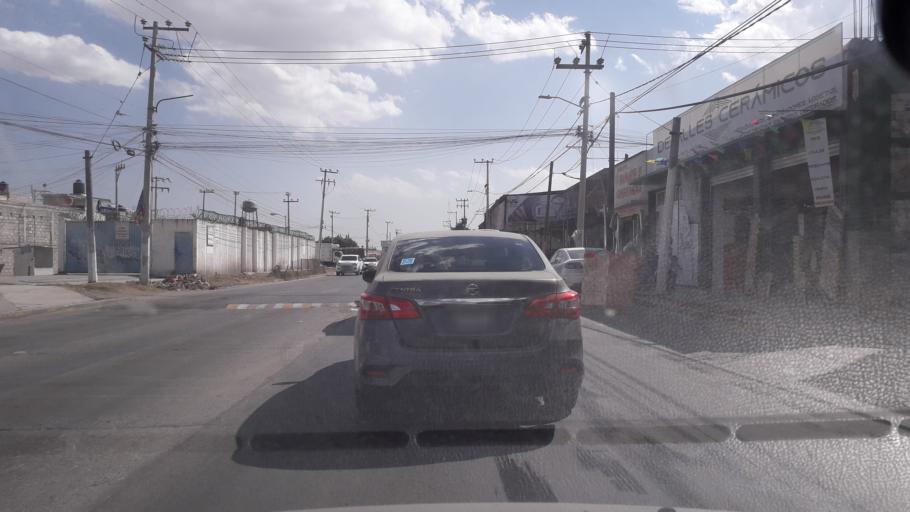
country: MX
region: Mexico
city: Ecatepec
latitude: 19.6290
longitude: -99.0512
